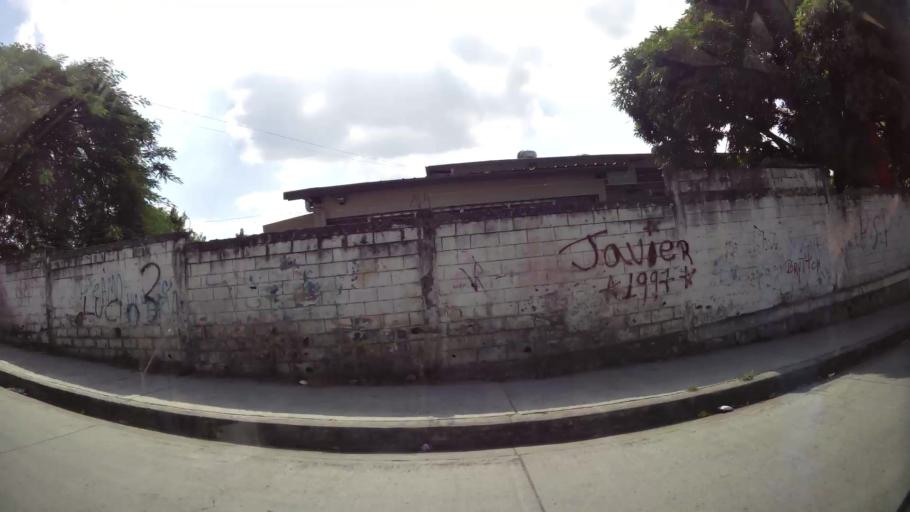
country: EC
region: Guayas
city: Santa Lucia
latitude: -2.1423
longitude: -79.9427
